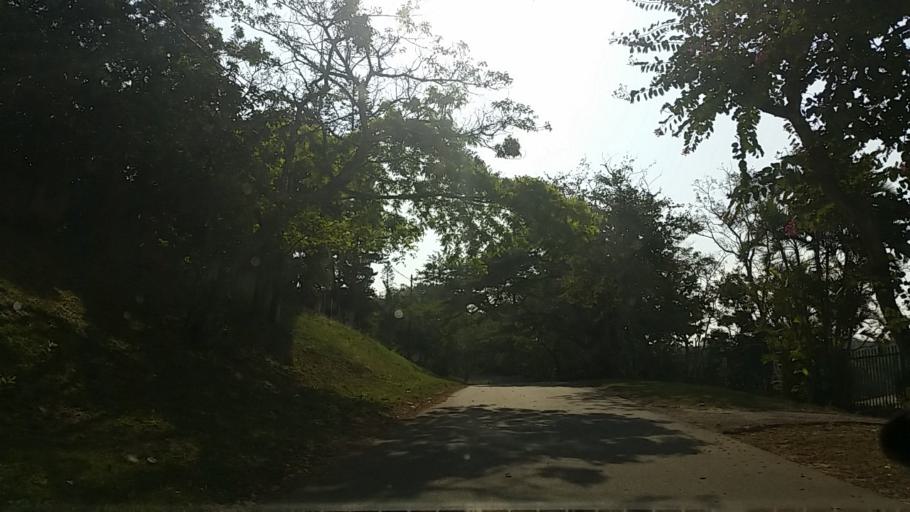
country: ZA
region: KwaZulu-Natal
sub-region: eThekwini Metropolitan Municipality
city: Berea
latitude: -29.8378
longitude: 30.9516
